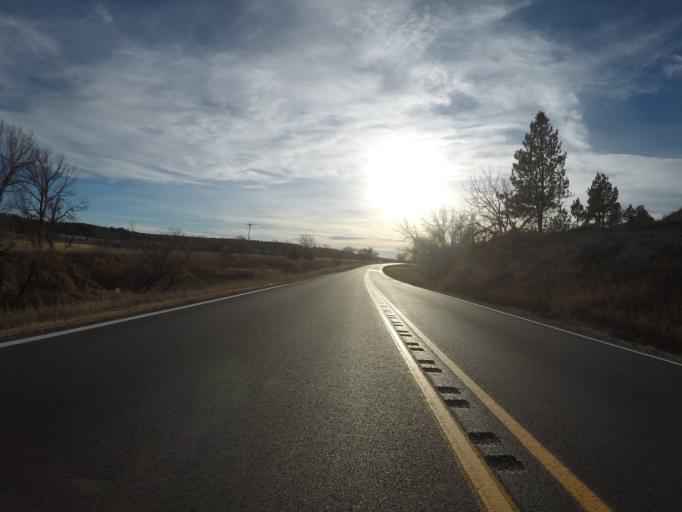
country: US
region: Montana
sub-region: Musselshell County
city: Roundup
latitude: 46.4049
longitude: -108.5971
